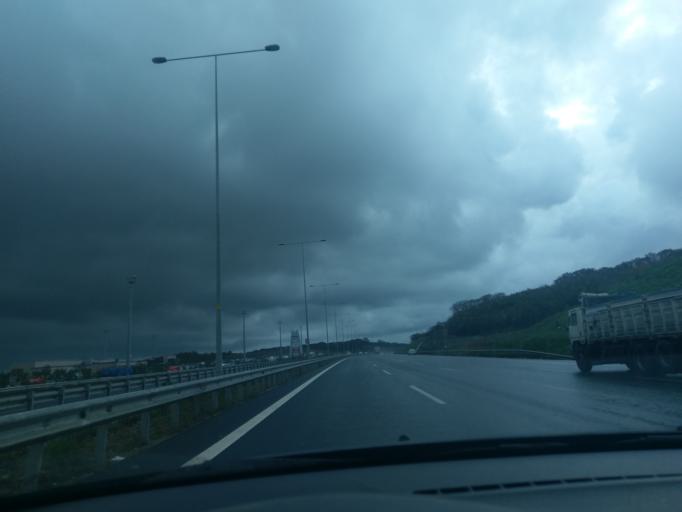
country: TR
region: Istanbul
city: Kemerburgaz
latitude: 41.2353
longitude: 28.9051
